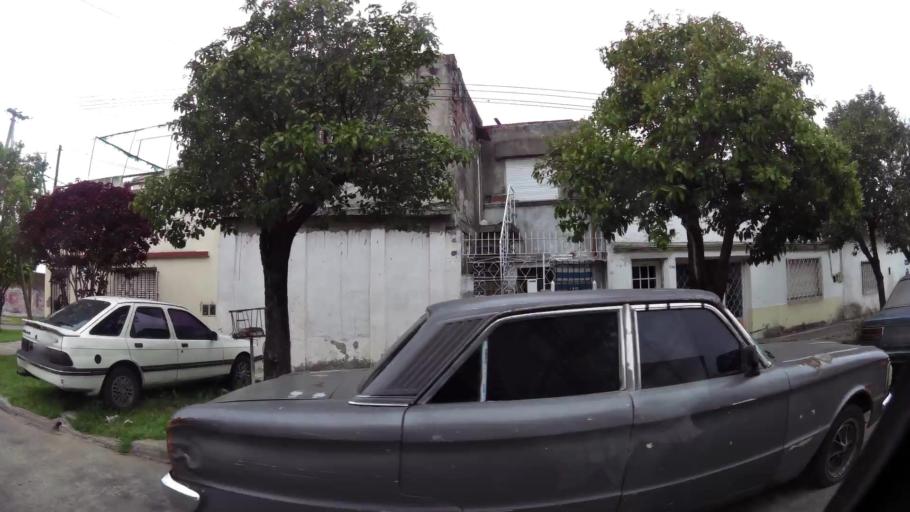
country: AR
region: Buenos Aires
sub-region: Partido de Lanus
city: Lanus
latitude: -34.6851
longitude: -58.3803
